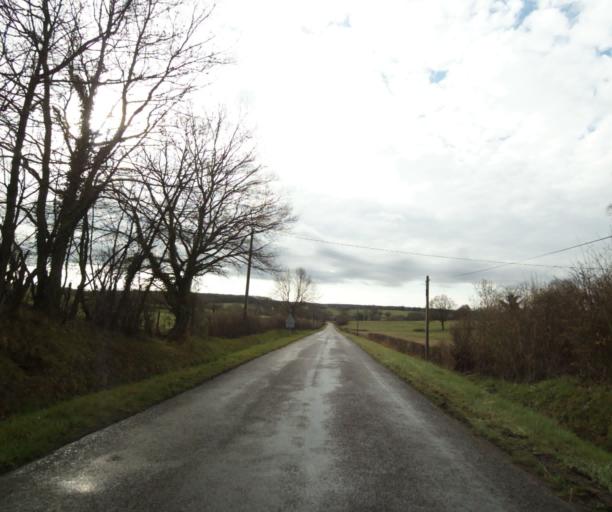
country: FR
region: Auvergne
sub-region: Departement de l'Allier
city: Toulon-sur-Allier
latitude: 46.5292
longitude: 3.4087
